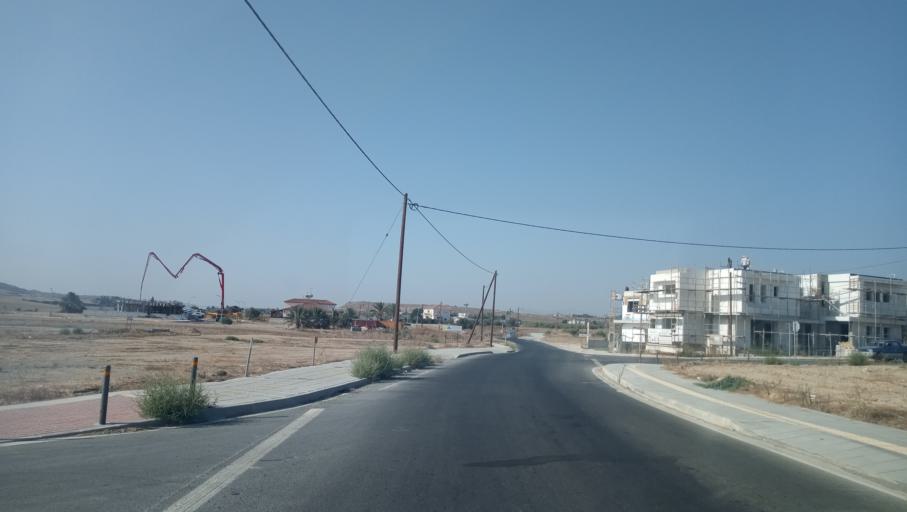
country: CY
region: Lefkosia
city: Geri
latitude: 35.0983
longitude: 33.4134
